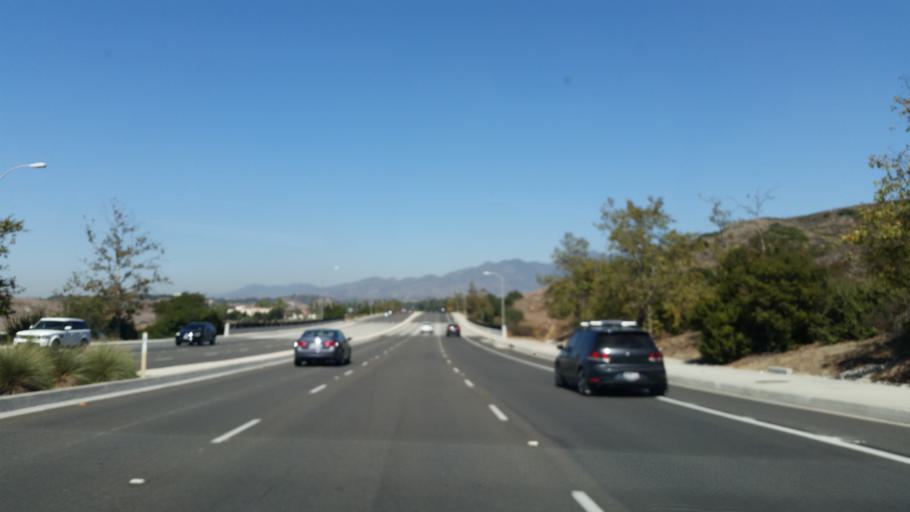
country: US
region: California
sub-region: Orange County
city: Ladera Ranch
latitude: 33.5755
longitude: -117.6330
